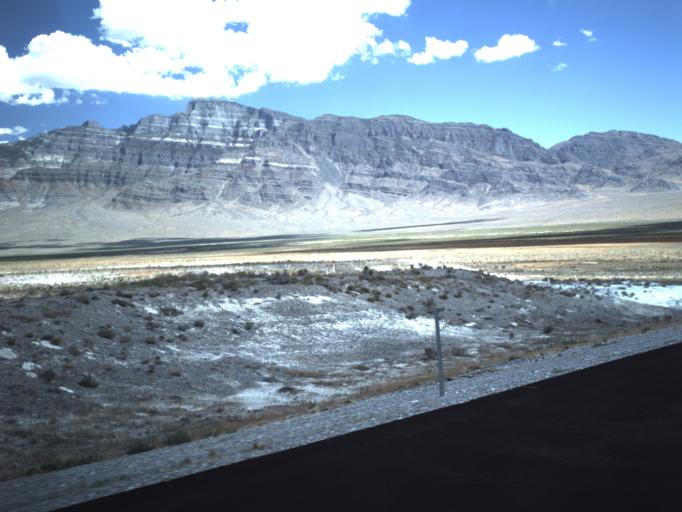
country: US
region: Utah
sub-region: Beaver County
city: Milford
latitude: 39.0839
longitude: -113.5017
